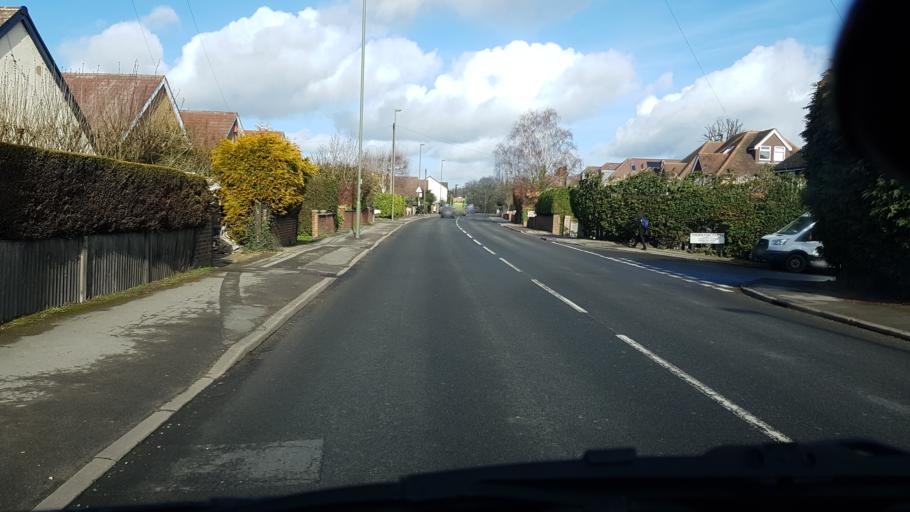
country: GB
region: England
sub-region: Surrey
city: Guildford
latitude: 51.2580
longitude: -0.5949
